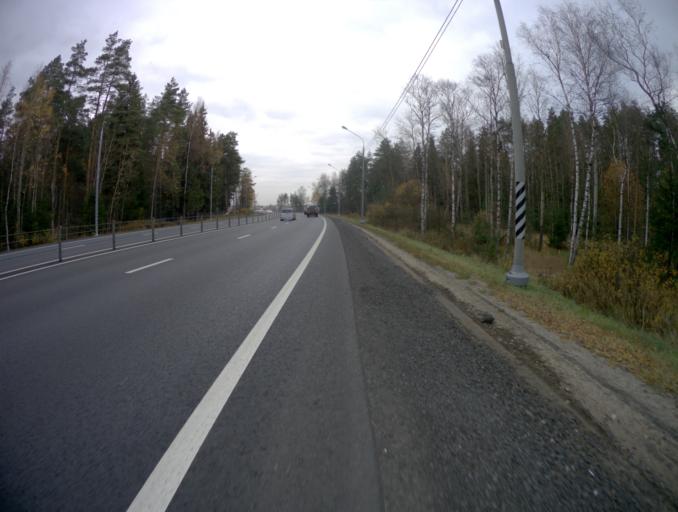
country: RU
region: Moskovskaya
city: Malaya Dubna
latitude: 55.8680
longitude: 38.9641
